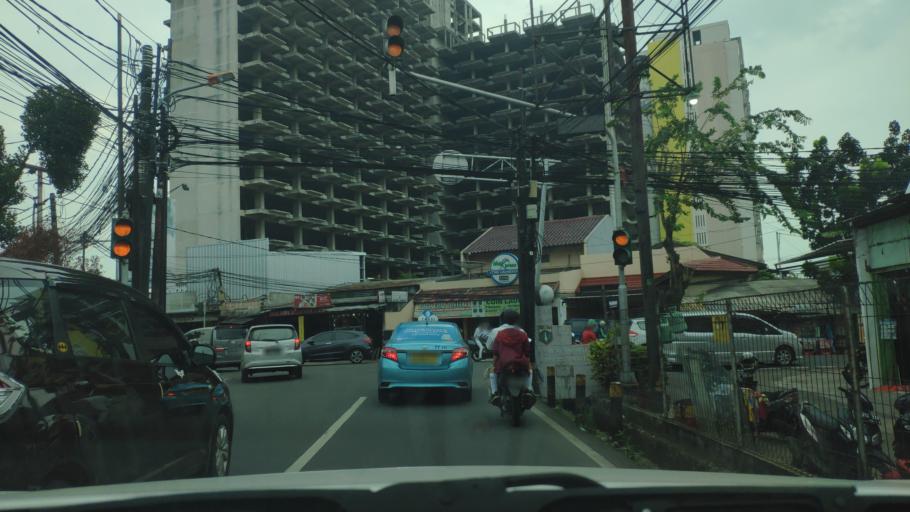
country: ID
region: Jakarta Raya
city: Jakarta
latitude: -6.1932
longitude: 106.7825
